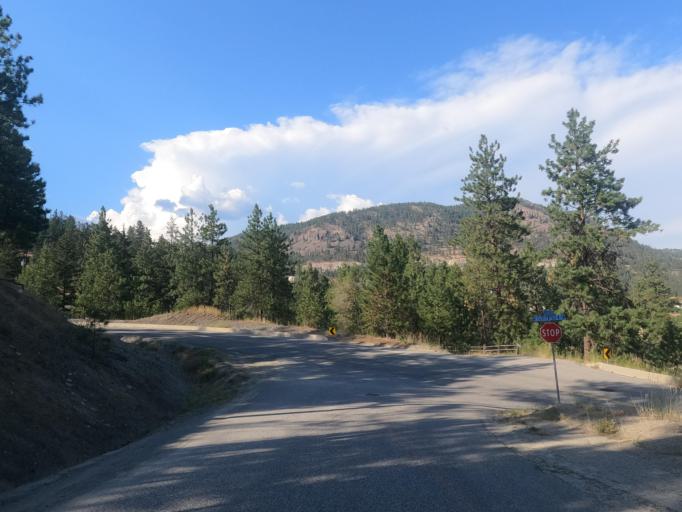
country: CA
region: British Columbia
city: Peachland
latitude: 49.7902
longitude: -119.7092
